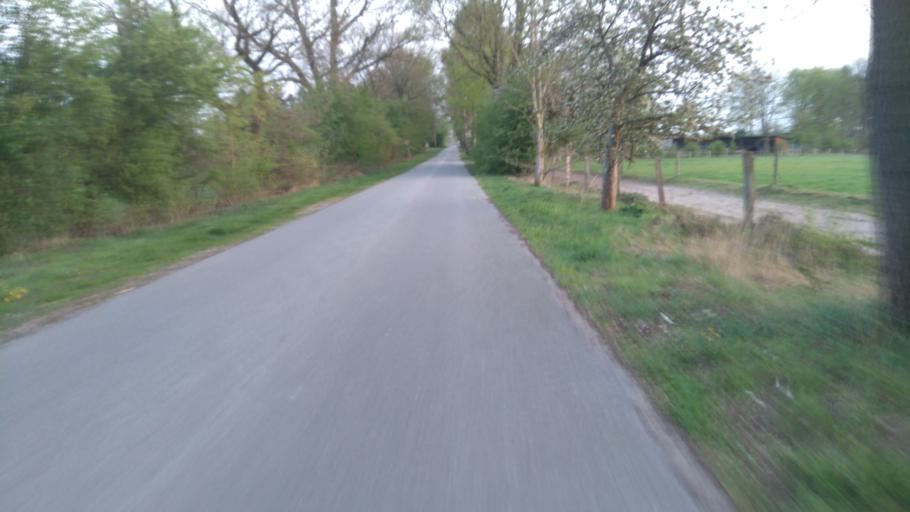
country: DE
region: Lower Saxony
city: Bargstedt
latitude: 53.4829
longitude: 9.4781
